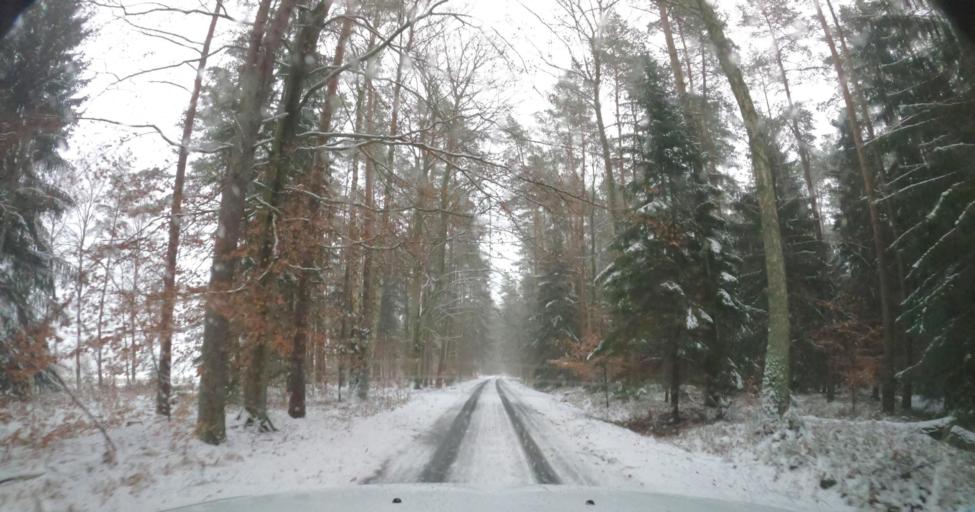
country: PL
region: West Pomeranian Voivodeship
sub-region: Powiat goleniowski
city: Przybiernow
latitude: 53.6616
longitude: 14.7834
